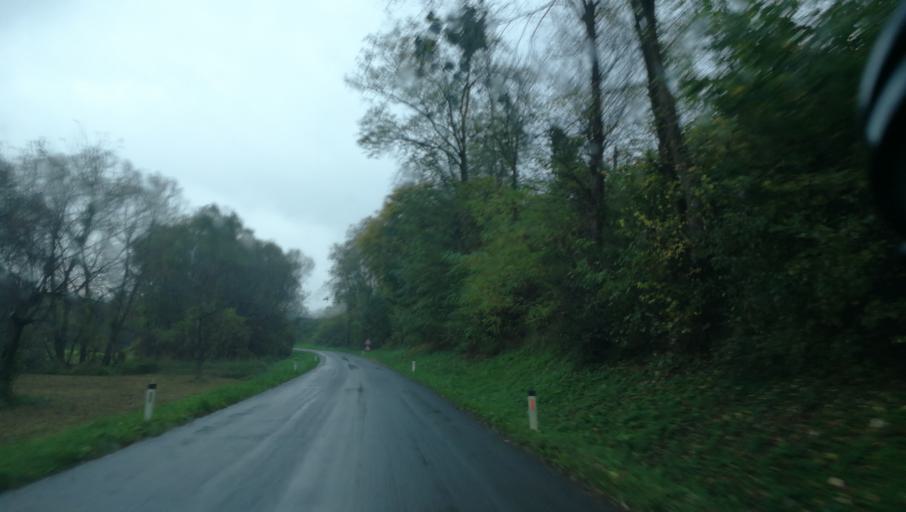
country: AT
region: Styria
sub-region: Politischer Bezirk Leibnitz
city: Spielfeld
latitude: 46.7122
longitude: 15.6254
